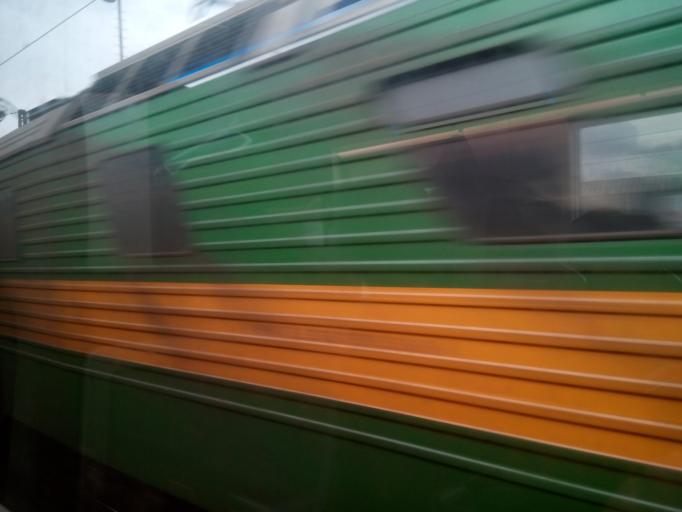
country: SK
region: Zilinsky
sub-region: Okres Zilina
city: Vrutky
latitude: 49.1077
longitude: 19.0321
